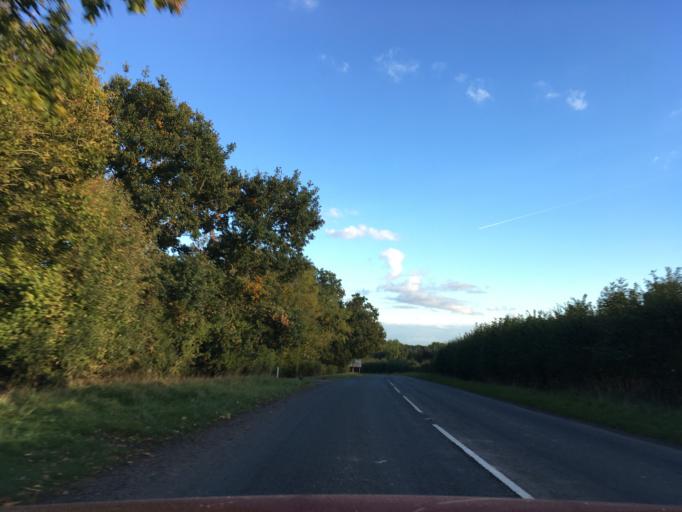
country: GB
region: England
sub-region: Herefordshire
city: Donnington
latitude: 52.0211
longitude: -2.3288
